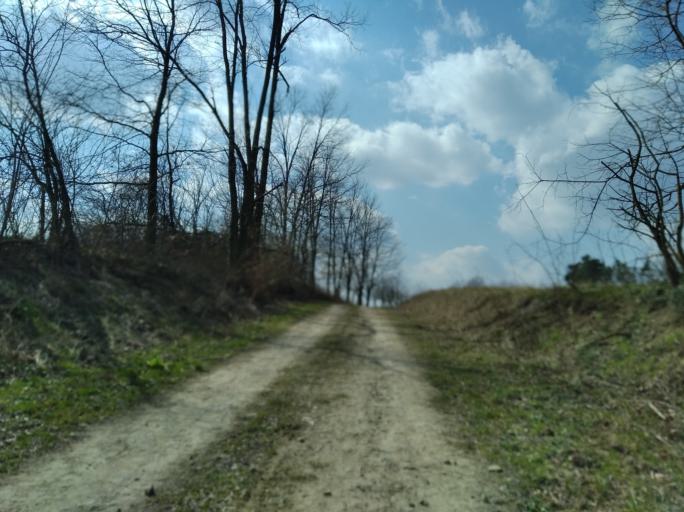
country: PL
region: Subcarpathian Voivodeship
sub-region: Powiat strzyzowski
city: Jawornik
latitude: 49.8238
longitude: 21.8570
